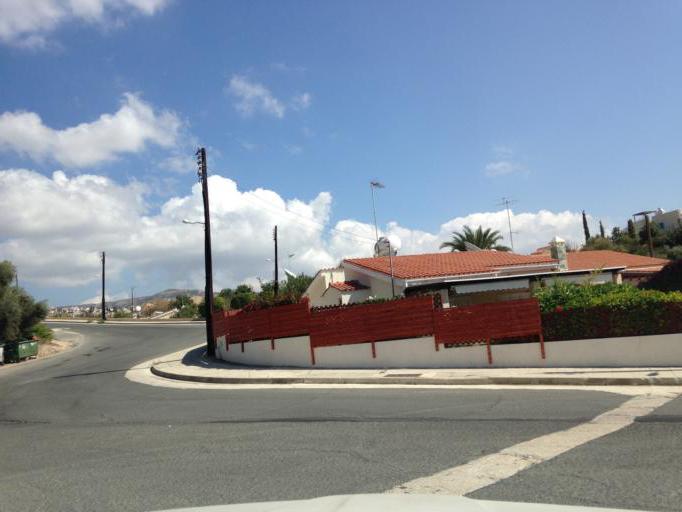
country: CY
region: Pafos
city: Pegeia
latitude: 34.8783
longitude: 32.3687
